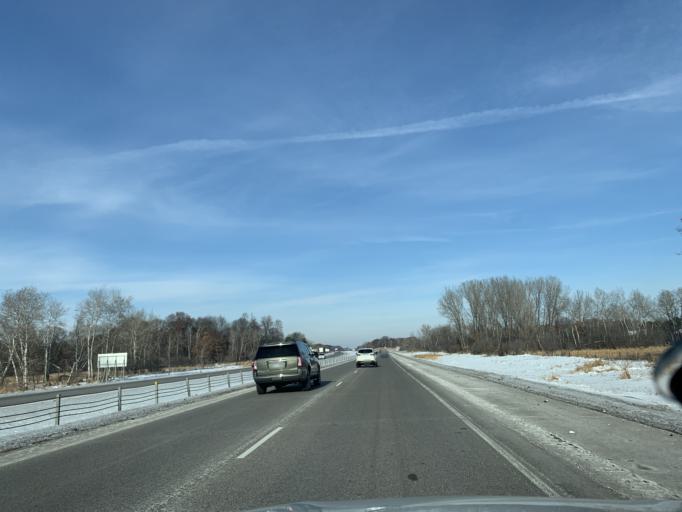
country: US
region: Minnesota
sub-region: Washington County
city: Forest Lake
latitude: 45.2990
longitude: -93.0025
